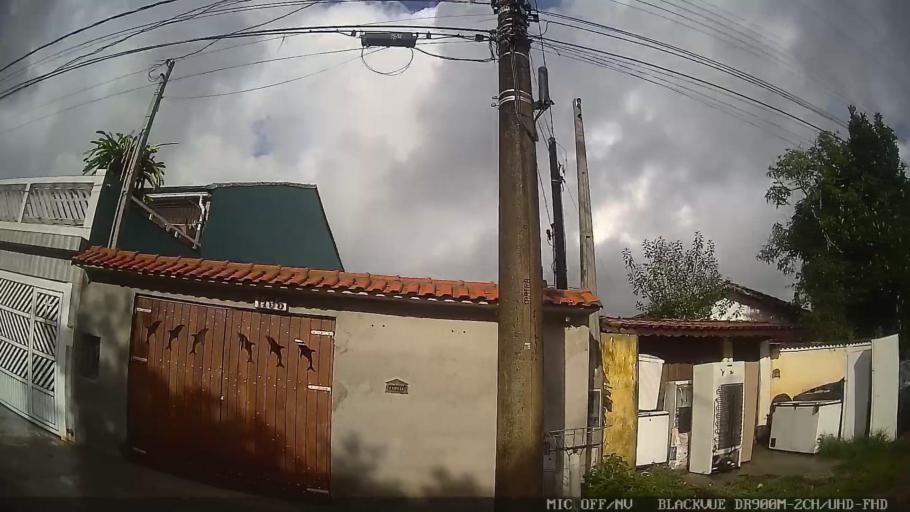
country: BR
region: Sao Paulo
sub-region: Itanhaem
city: Itanhaem
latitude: -24.2248
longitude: -46.8900
